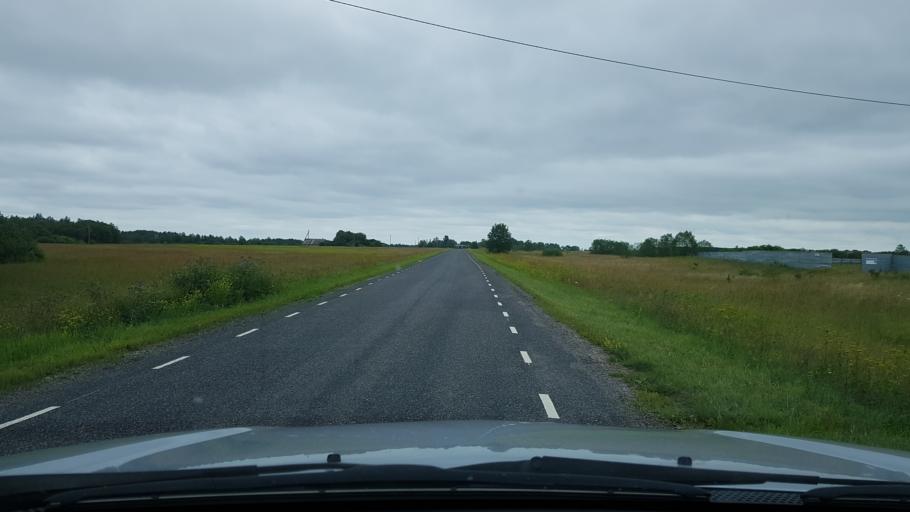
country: EE
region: Ida-Virumaa
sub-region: Narva linn
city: Narva
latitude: 59.3778
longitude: 28.1221
